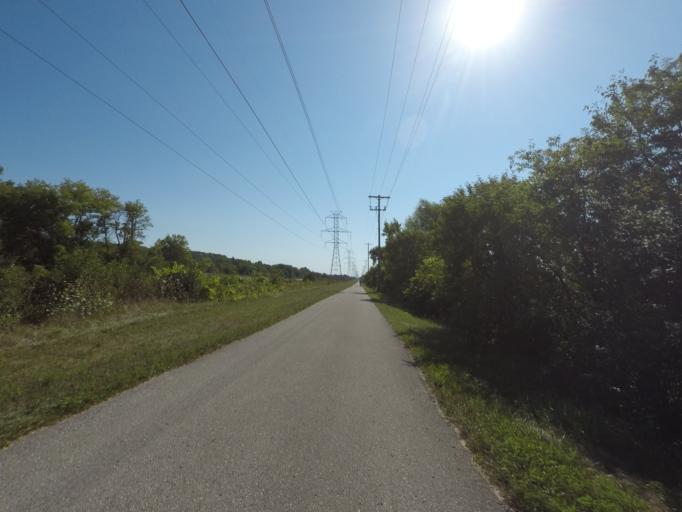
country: US
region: Wisconsin
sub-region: Waukesha County
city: Waukesha
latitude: 43.0099
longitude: -88.1666
